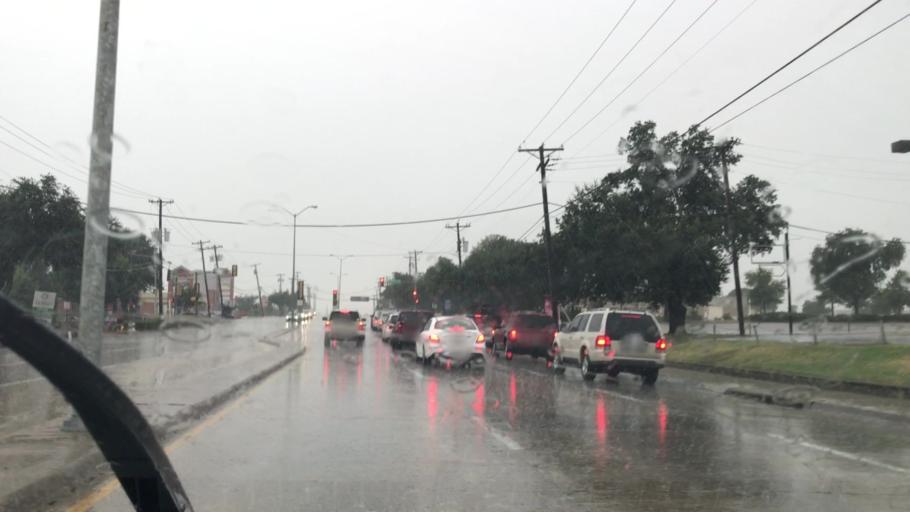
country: US
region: Texas
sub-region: Dallas County
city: Addison
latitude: 32.9310
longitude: -96.8036
